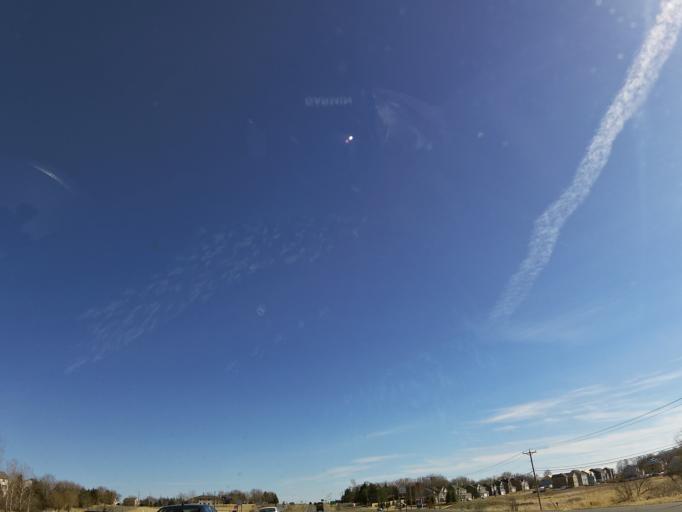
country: US
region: Minnesota
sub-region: Hennepin County
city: Corcoran
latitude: 45.0392
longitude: -93.5180
